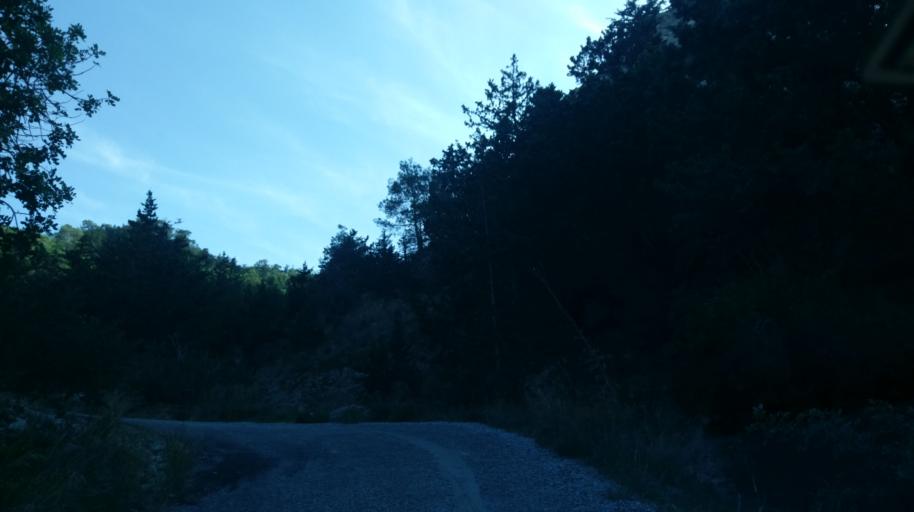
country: CY
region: Ammochostos
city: Lefkonoiko
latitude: 35.3345
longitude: 33.6318
